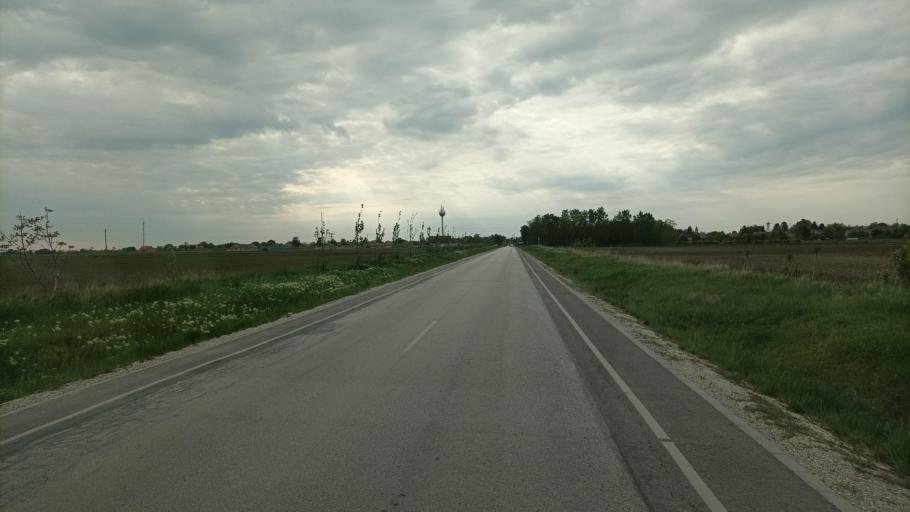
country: HU
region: Pest
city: Nyaregyhaza
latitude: 47.2682
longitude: 19.4935
